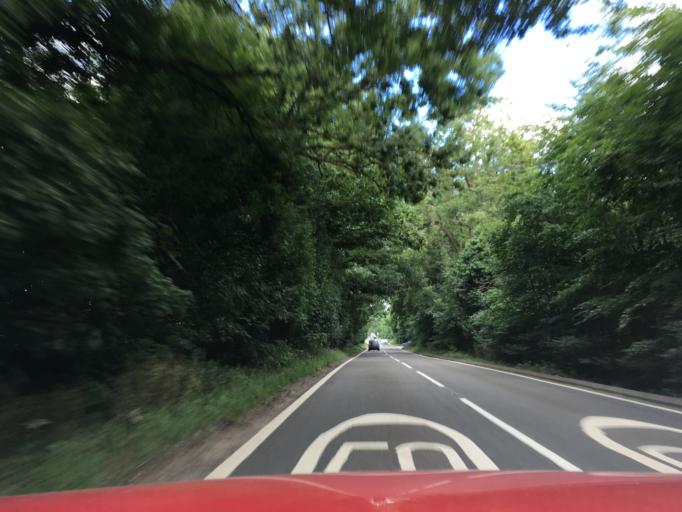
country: GB
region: England
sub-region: Leicestershire
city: Measham
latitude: 52.6544
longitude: -1.5314
